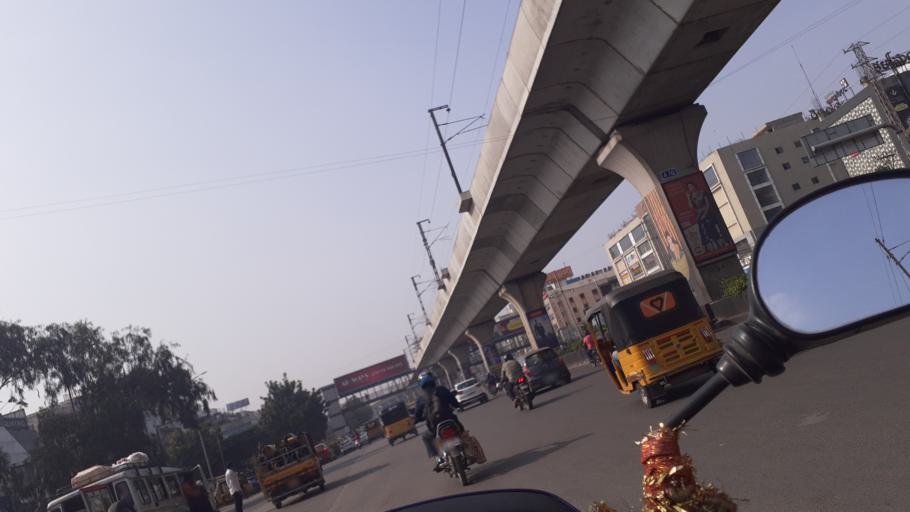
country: IN
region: Telangana
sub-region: Rangareddi
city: Kukatpalli
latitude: 17.4924
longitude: 78.4048
